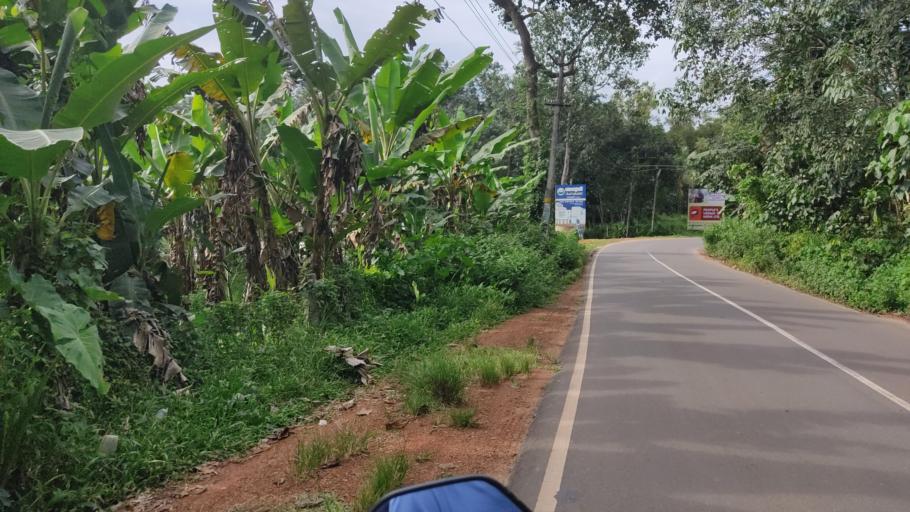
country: IN
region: Kerala
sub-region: Pattanamtitta
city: Adur
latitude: 9.1936
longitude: 76.7760
